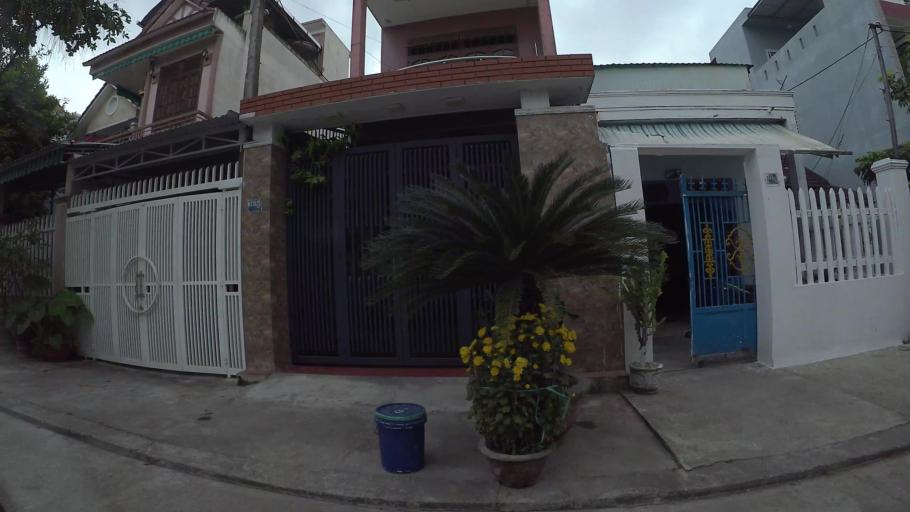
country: VN
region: Da Nang
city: Cam Le
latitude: 16.0370
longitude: 108.1737
